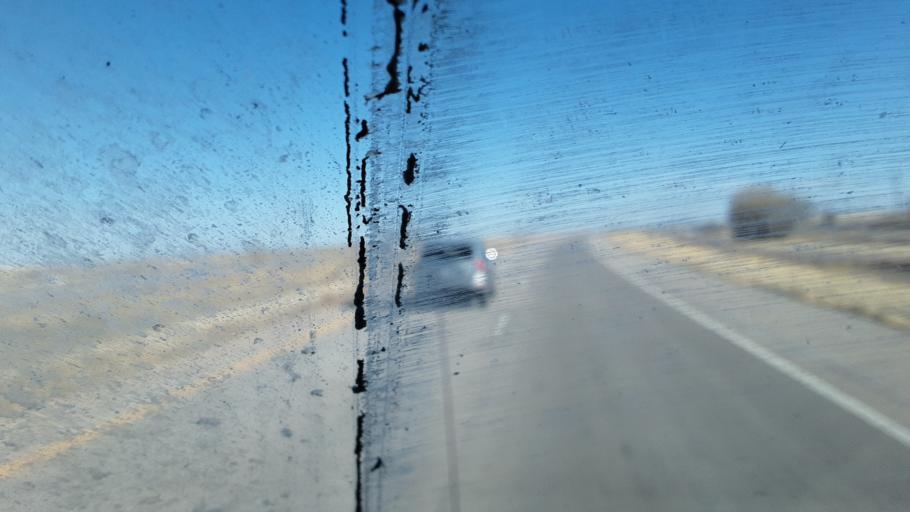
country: US
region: Colorado
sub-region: Weld County
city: Keenesburg
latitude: 40.1105
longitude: -104.5697
